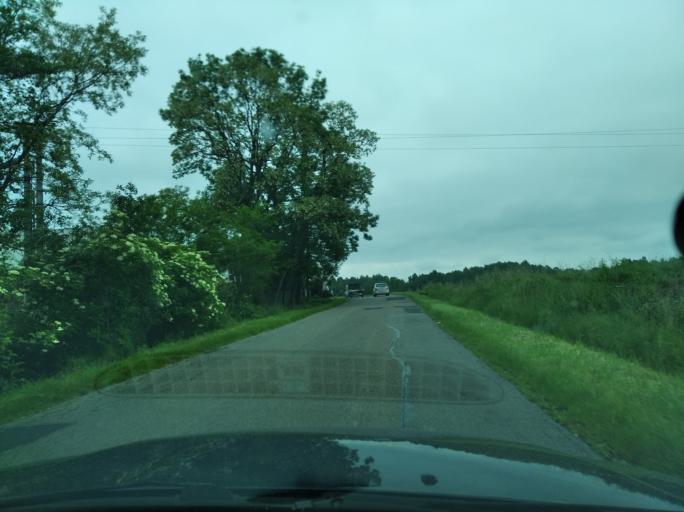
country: PL
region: Subcarpathian Voivodeship
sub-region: Powiat kolbuszowski
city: Niwiska
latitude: 50.1614
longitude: 21.6677
